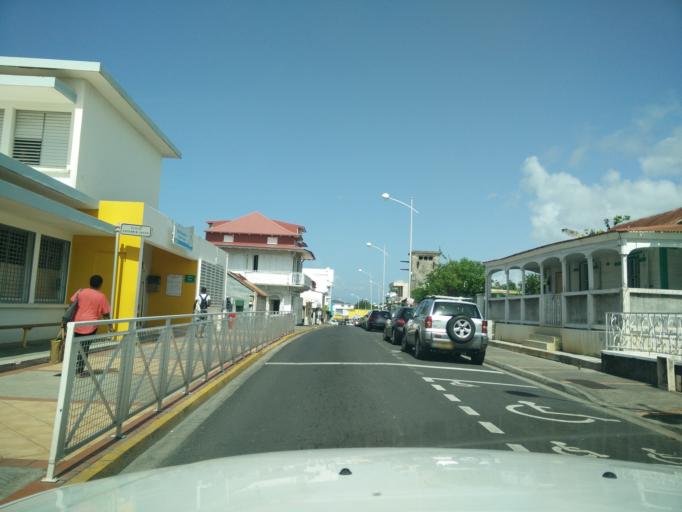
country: GP
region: Guadeloupe
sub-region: Guadeloupe
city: Le Gosier
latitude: 16.2059
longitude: -61.4897
